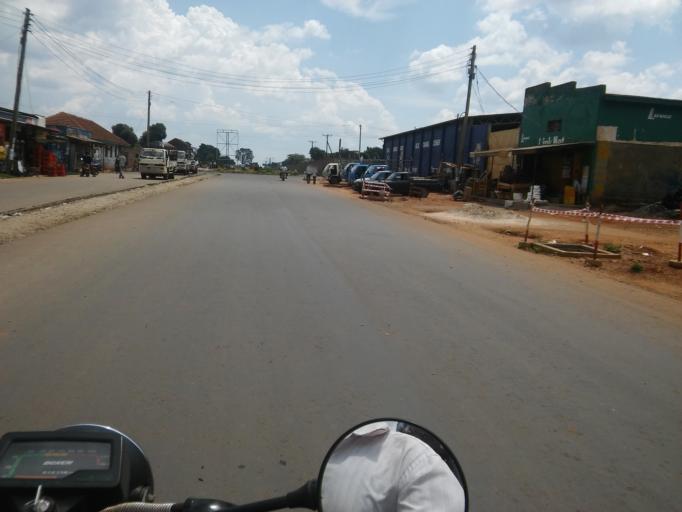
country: UG
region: Eastern Region
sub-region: Mbale District
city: Mbale
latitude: 1.0763
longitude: 34.1609
